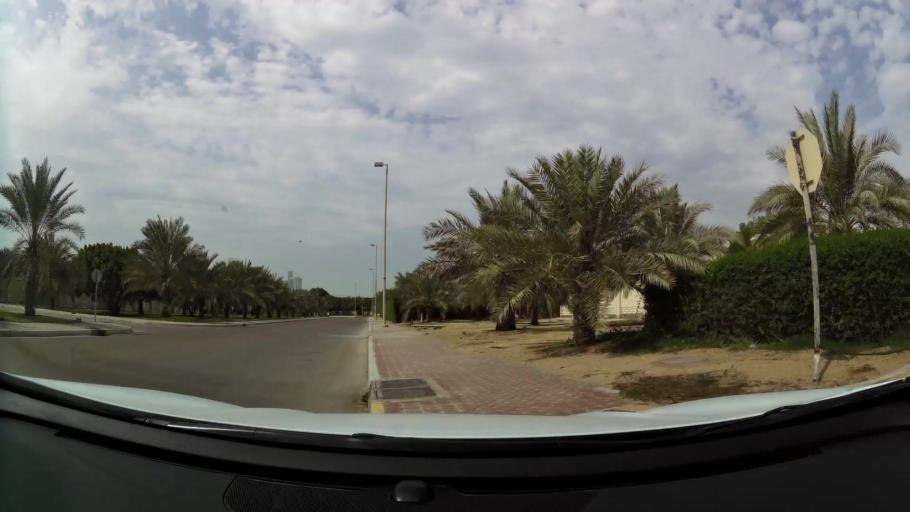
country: AE
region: Abu Dhabi
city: Abu Dhabi
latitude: 24.4481
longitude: 54.3495
